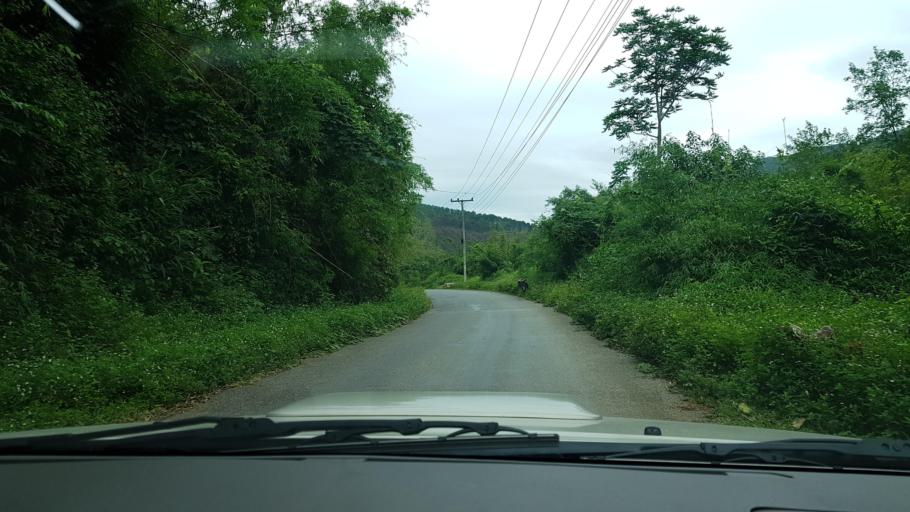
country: LA
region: Phongsali
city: Khoa
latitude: 21.0498
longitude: 102.4084
